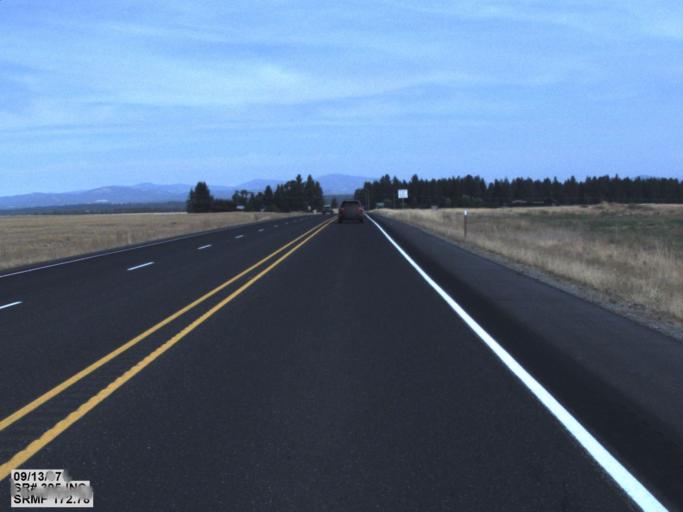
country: US
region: Washington
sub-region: Spokane County
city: Fairwood
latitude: 47.8555
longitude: -117.4219
